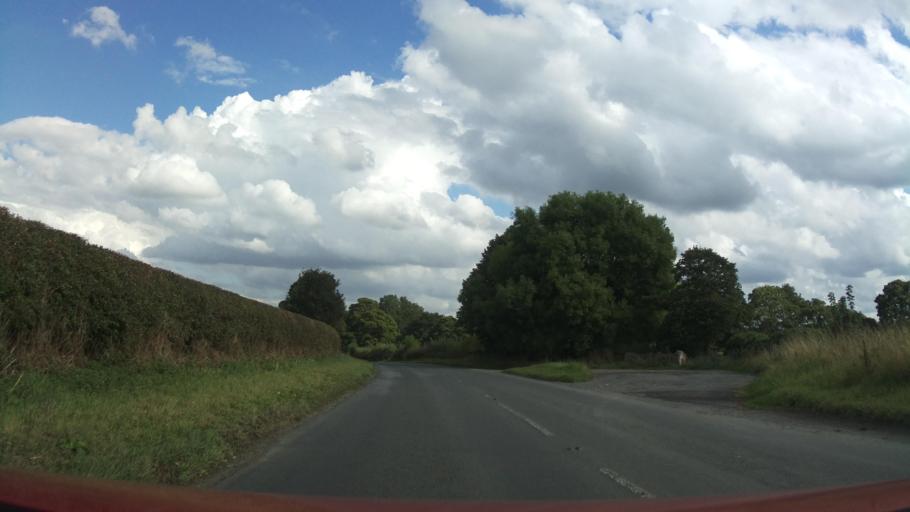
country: GB
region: England
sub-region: North Yorkshire
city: Leyburn
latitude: 54.2687
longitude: -1.7702
